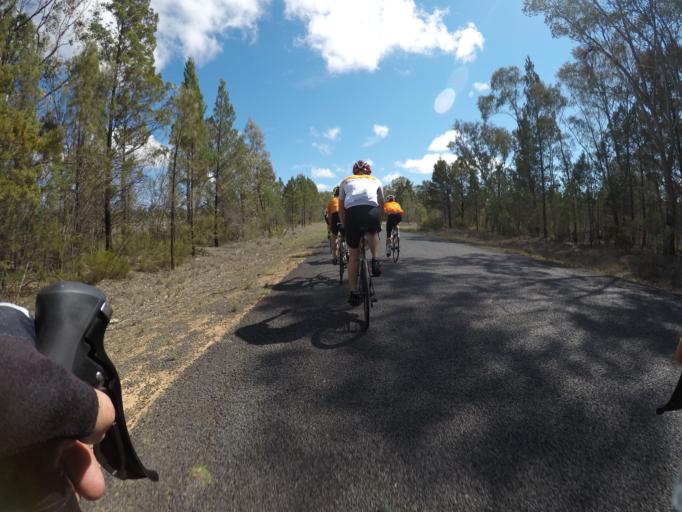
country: AU
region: New South Wales
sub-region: Parkes
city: Peak Hill
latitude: -32.6261
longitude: 148.5490
